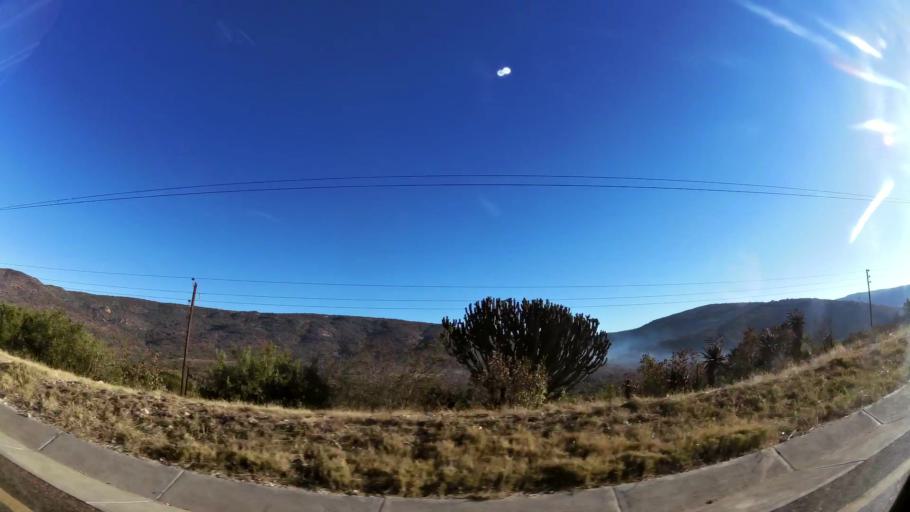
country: ZA
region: Limpopo
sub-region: Capricorn District Municipality
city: Mankoeng
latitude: -23.9347
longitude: 29.8357
